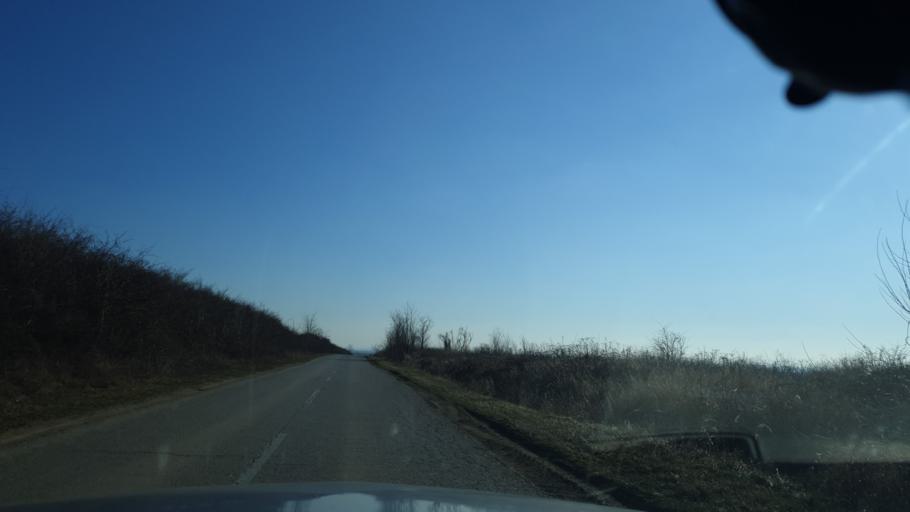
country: RS
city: Vrdnik
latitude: 45.0950
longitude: 19.8053
